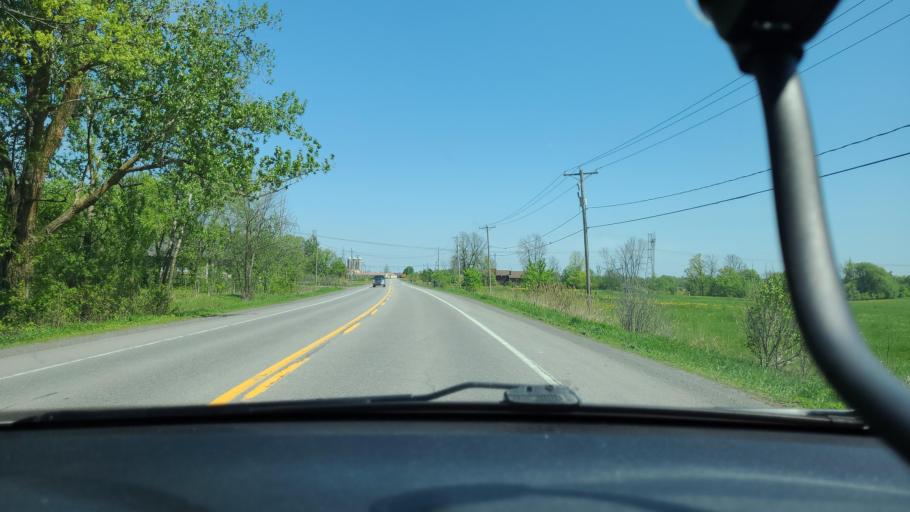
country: CA
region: Quebec
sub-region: Laurentides
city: Mirabel
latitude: 45.6018
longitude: -74.0534
